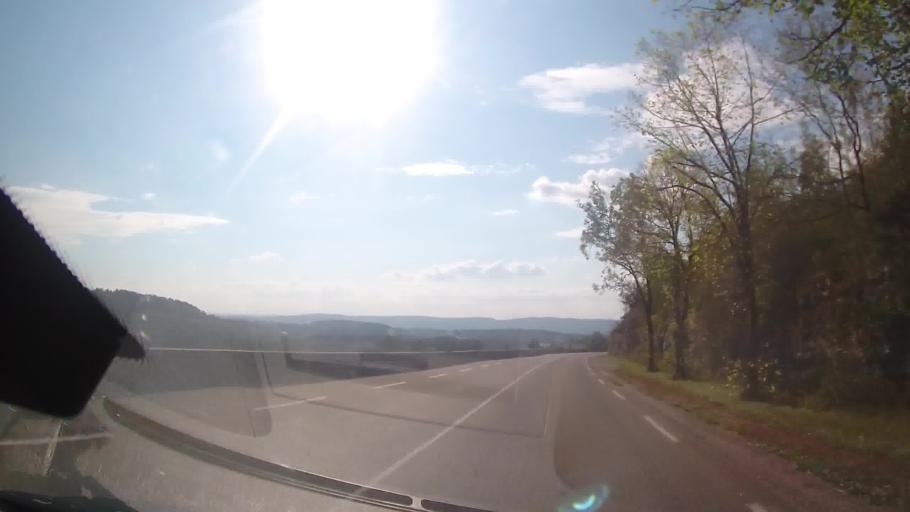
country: FR
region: Franche-Comte
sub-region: Departement du Jura
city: Clairvaux-les-Lacs
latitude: 46.5802
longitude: 5.7777
